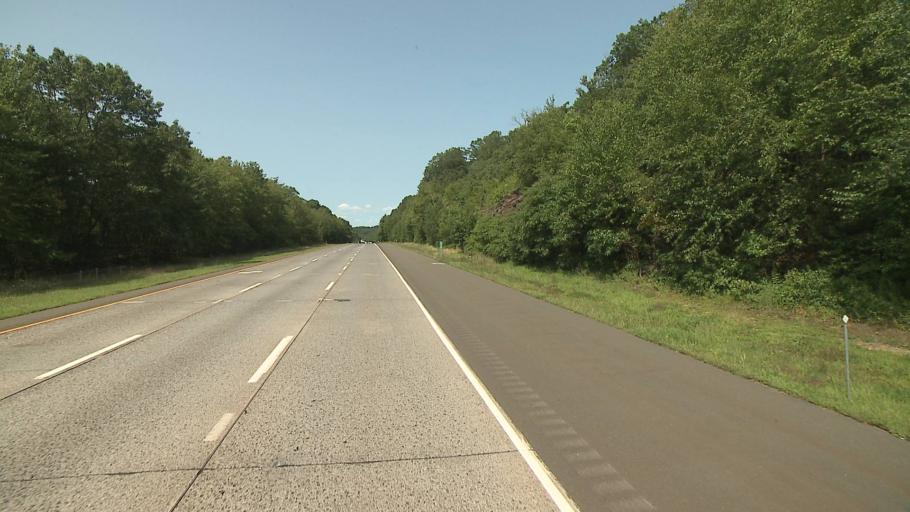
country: US
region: Connecticut
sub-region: Fairfield County
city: Trumbull
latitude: 41.2653
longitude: -73.2098
